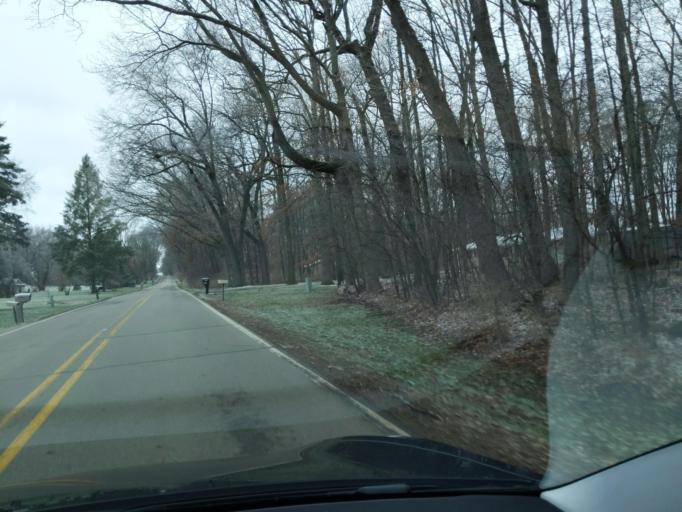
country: US
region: Michigan
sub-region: Jackson County
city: Spring Arbor
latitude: 42.1983
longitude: -84.5377
